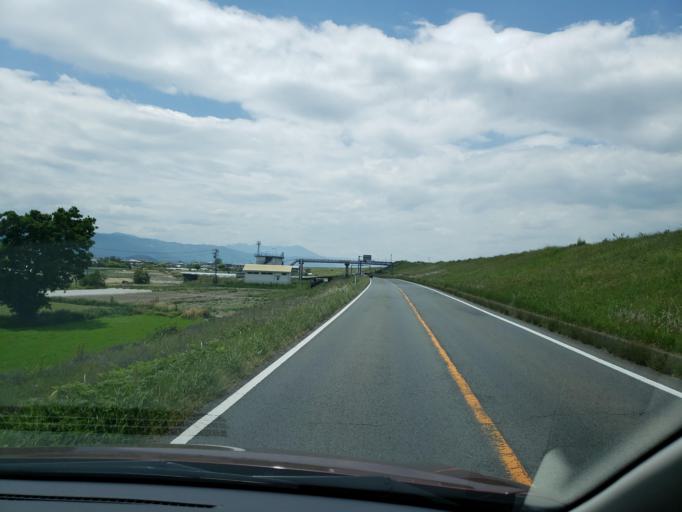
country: JP
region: Tokushima
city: Ishii
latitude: 34.1012
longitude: 134.4331
